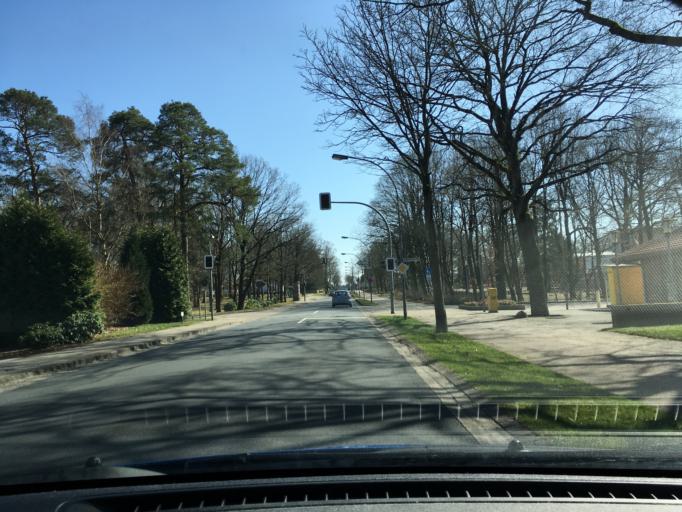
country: DE
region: Lower Saxony
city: Unterluss
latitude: 52.8439
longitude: 10.2944
